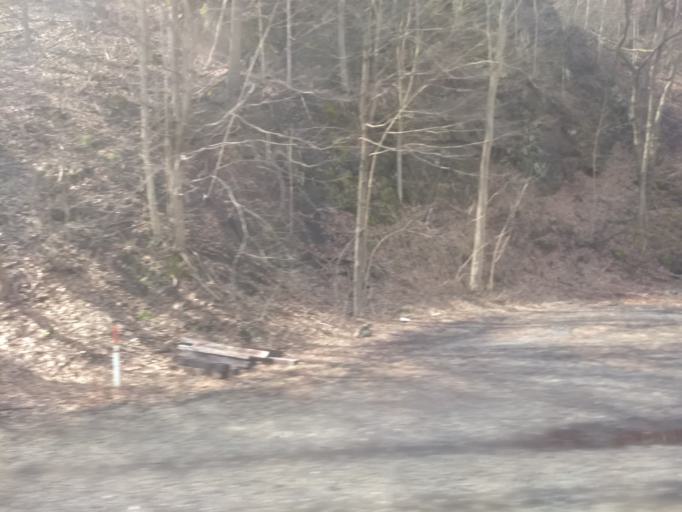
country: US
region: Pennsylvania
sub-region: Blair County
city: Tyrone
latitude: 40.6385
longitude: -78.1937
